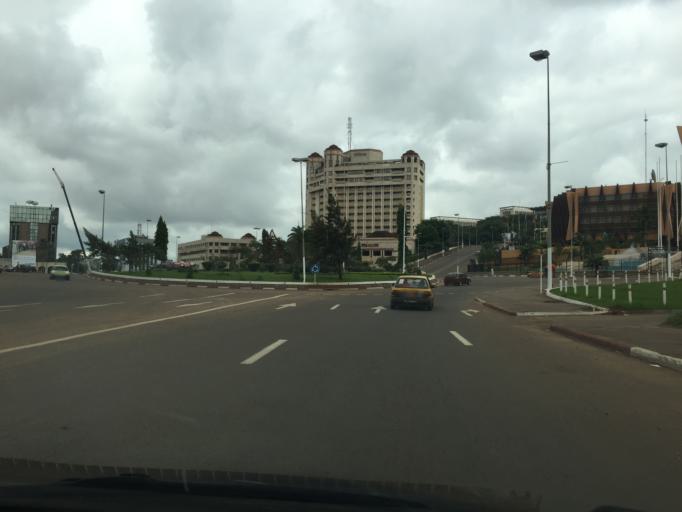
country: CM
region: Centre
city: Yaounde
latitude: 3.8670
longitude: 11.5149
